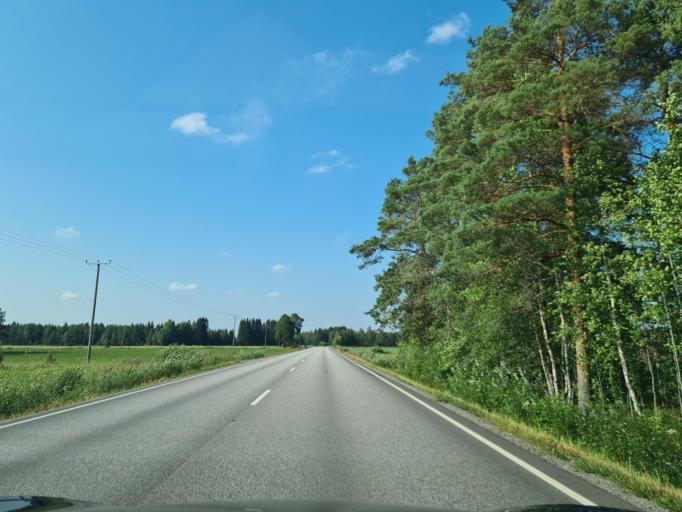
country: FI
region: Satakunta
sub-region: Pohjois-Satakunta
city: Karvia
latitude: 62.0524
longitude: 22.5143
